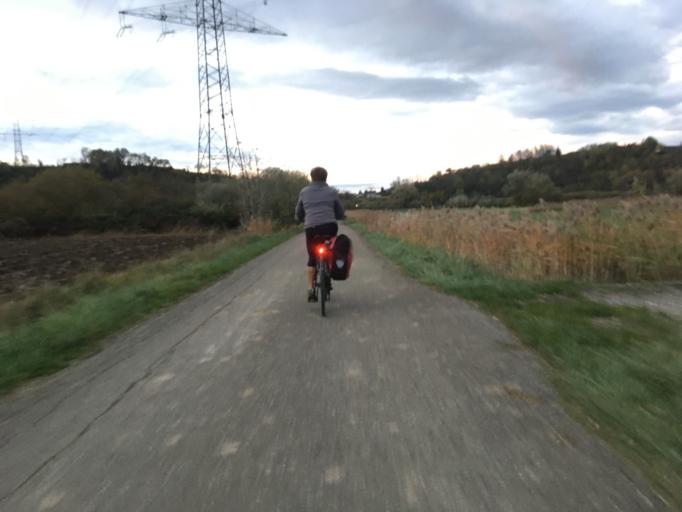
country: DE
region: Baden-Wuerttemberg
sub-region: Freiburg Region
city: Riegel
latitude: 48.1381
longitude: 7.7441
